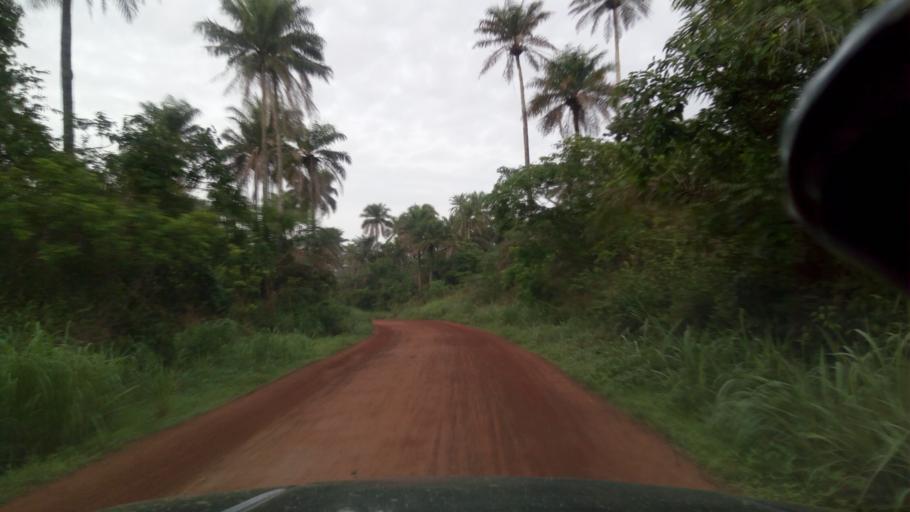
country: SL
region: Northern Province
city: Port Loko
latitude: 8.7368
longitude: -12.7968
